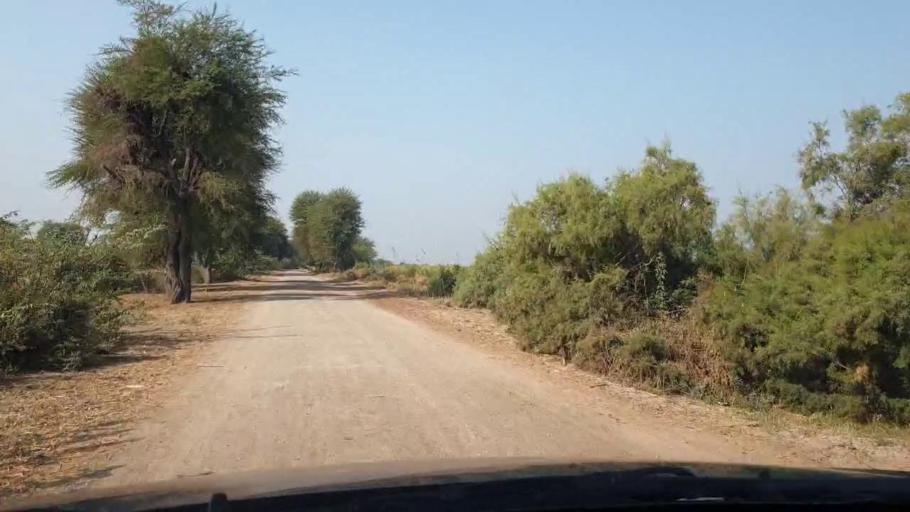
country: PK
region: Sindh
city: Jhol
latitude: 25.9600
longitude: 68.9301
